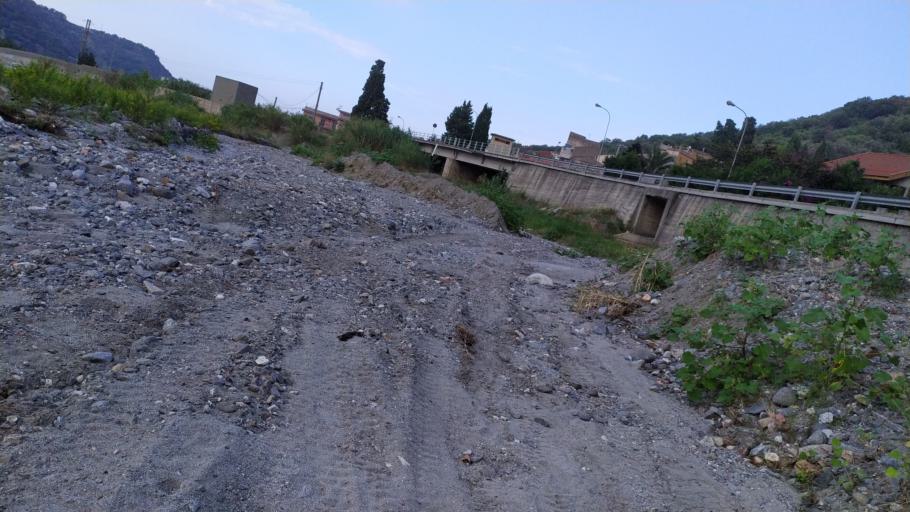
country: IT
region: Sicily
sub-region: Messina
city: Saponara
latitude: 38.2023
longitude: 15.4305
